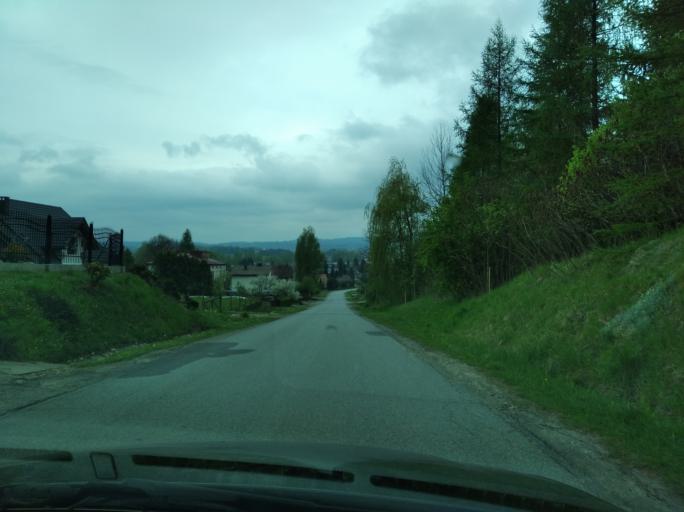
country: PL
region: Subcarpathian Voivodeship
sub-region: Powiat sanocki
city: Sanok
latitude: 49.5565
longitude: 22.2313
